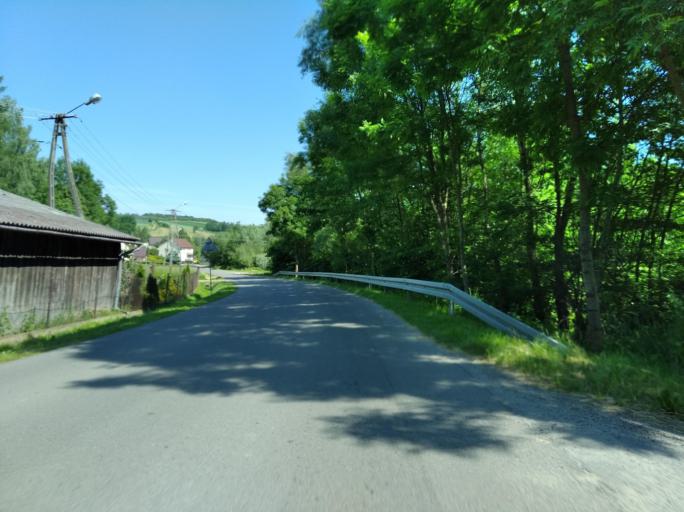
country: PL
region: Subcarpathian Voivodeship
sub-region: Powiat ropczycko-sedziszowski
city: Zagorzyce
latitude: 50.0052
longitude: 21.6584
